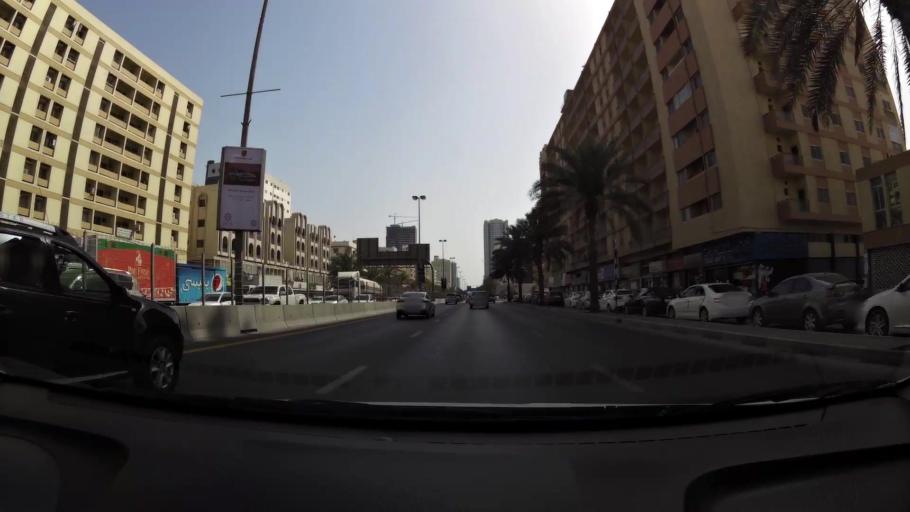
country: AE
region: Ash Shariqah
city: Sharjah
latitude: 25.3181
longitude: 55.3857
